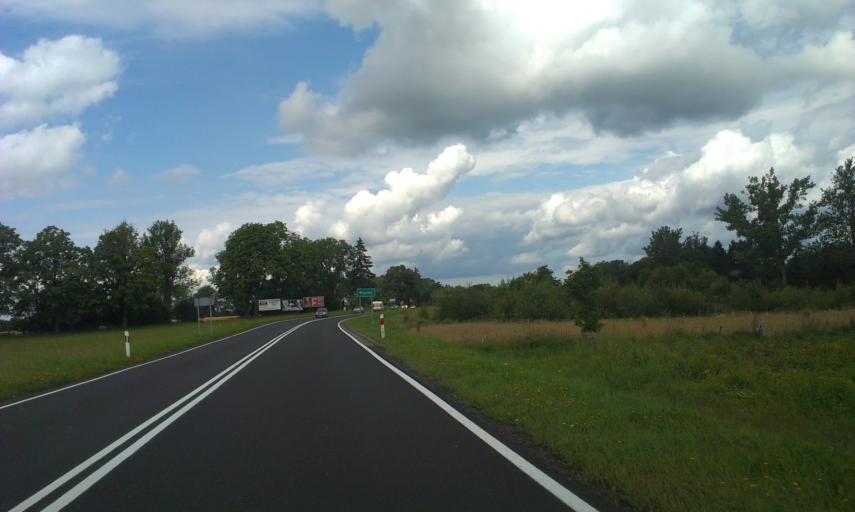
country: PL
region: West Pomeranian Voivodeship
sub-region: Powiat koszalinski
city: Bobolice
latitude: 54.0257
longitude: 16.4677
